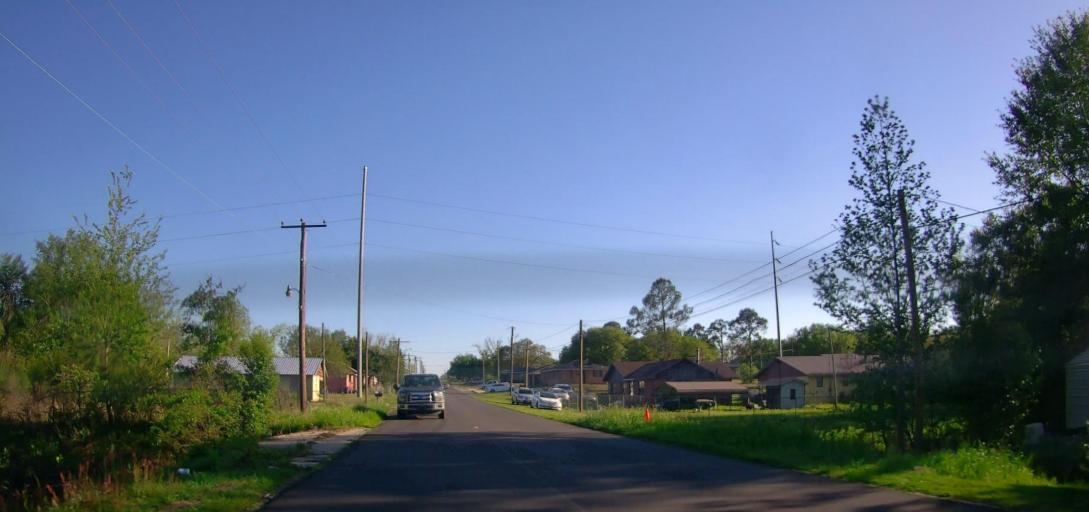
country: US
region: Georgia
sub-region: Ben Hill County
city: Fitzgerald
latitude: 31.7214
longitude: -83.2440
